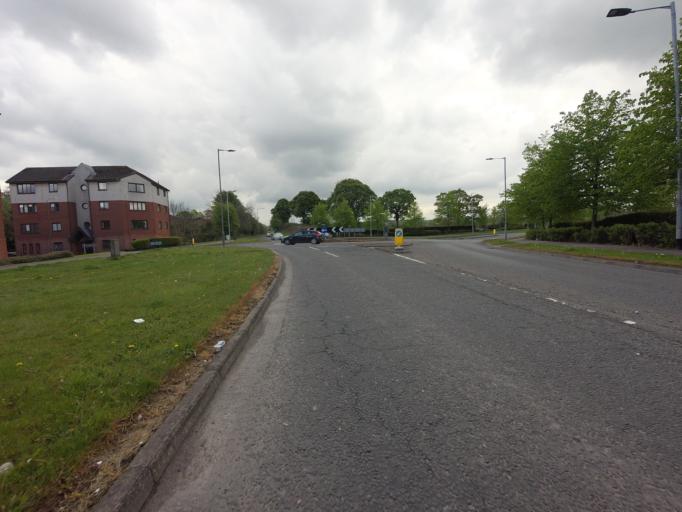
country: GB
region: Scotland
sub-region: Falkirk
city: Falkirk
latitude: 56.0127
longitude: -3.7964
